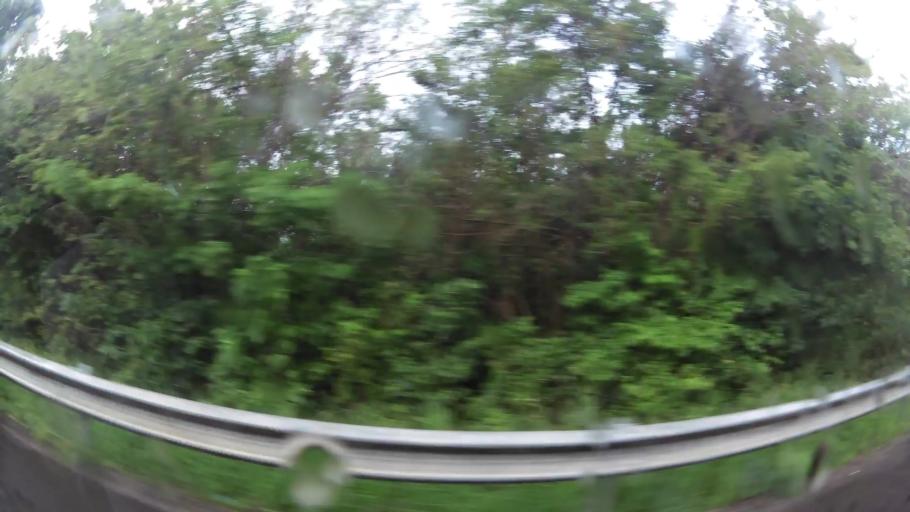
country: MQ
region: Martinique
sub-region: Martinique
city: Sainte-Luce
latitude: 14.4712
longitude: -60.9487
